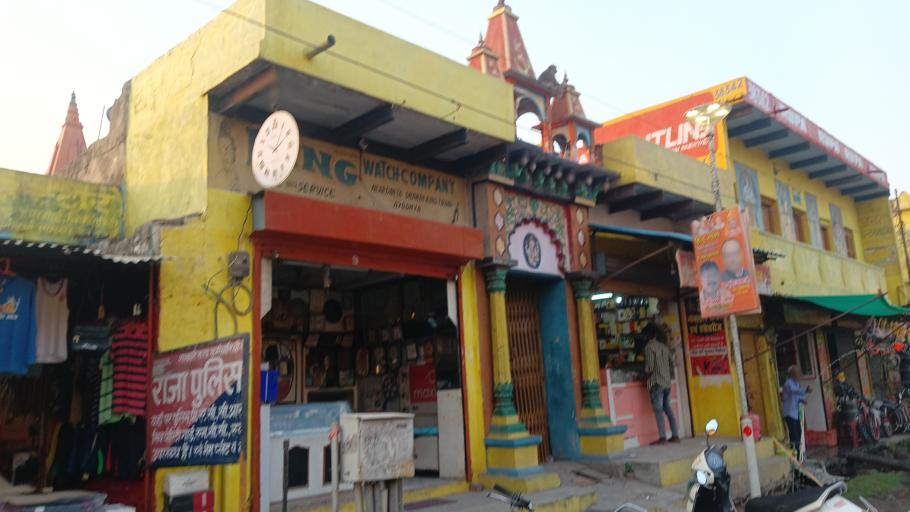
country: IN
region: Uttar Pradesh
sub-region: Faizabad
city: Ayodhya
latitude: 26.7943
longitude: 82.2019
